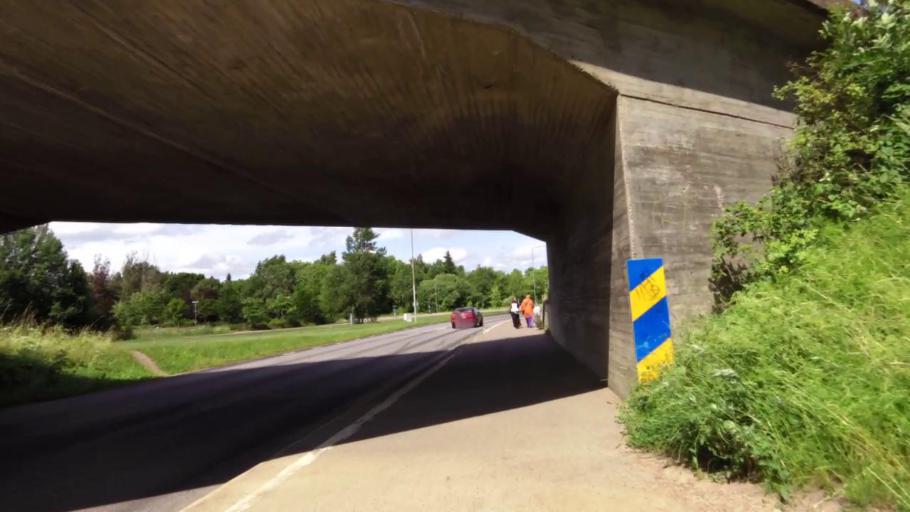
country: SE
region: OEstergoetland
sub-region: Linkopings Kommun
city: Malmslatt
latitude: 58.4217
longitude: 15.5658
